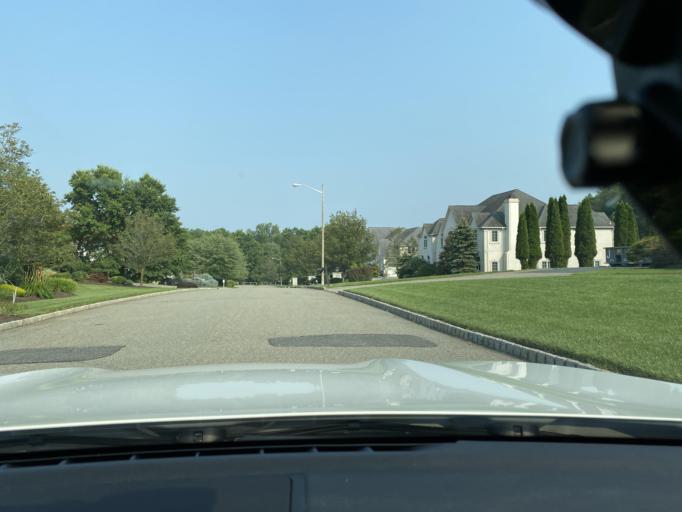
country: US
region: New Jersey
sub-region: Bergen County
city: Mahwah
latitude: 41.0846
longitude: -74.1257
